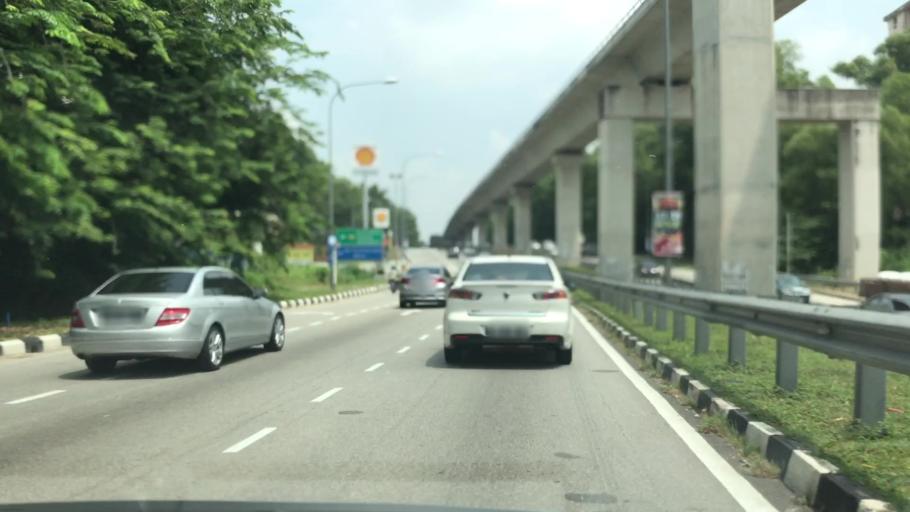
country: MY
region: Selangor
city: Subang Jaya
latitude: 3.0493
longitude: 101.6345
